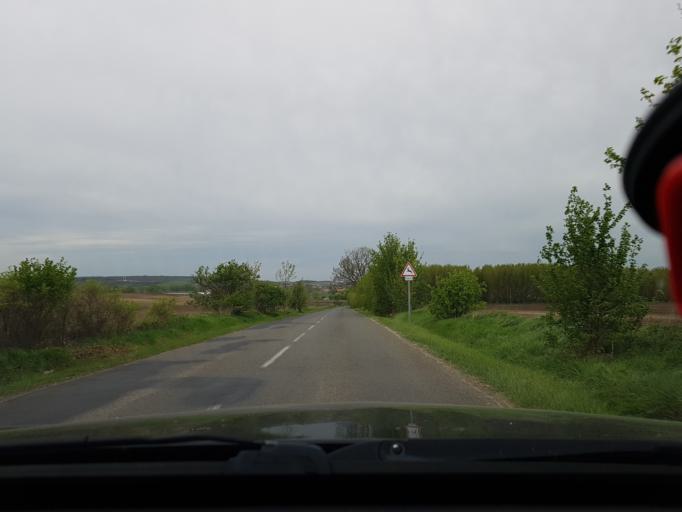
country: HU
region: Pest
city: Perbal
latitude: 47.5766
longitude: 18.7779
